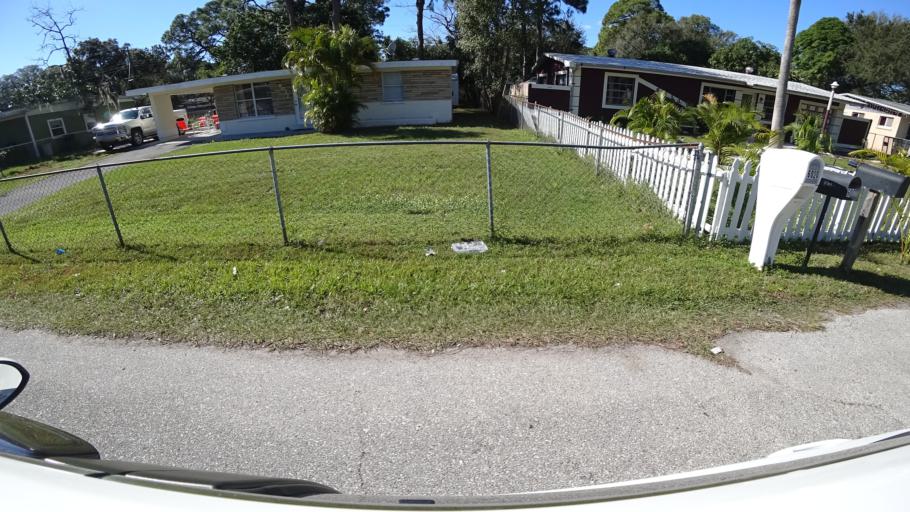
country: US
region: Florida
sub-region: Manatee County
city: Whitfield
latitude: 27.4337
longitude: -82.5544
